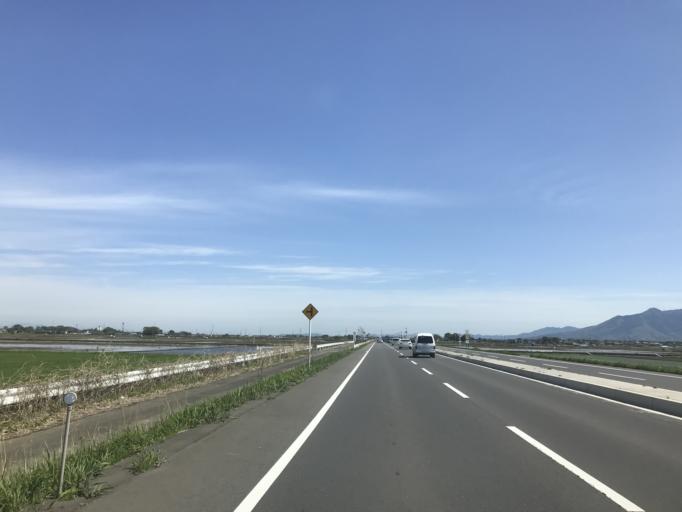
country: JP
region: Ibaraki
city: Ishige
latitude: 36.1338
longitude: 139.9844
